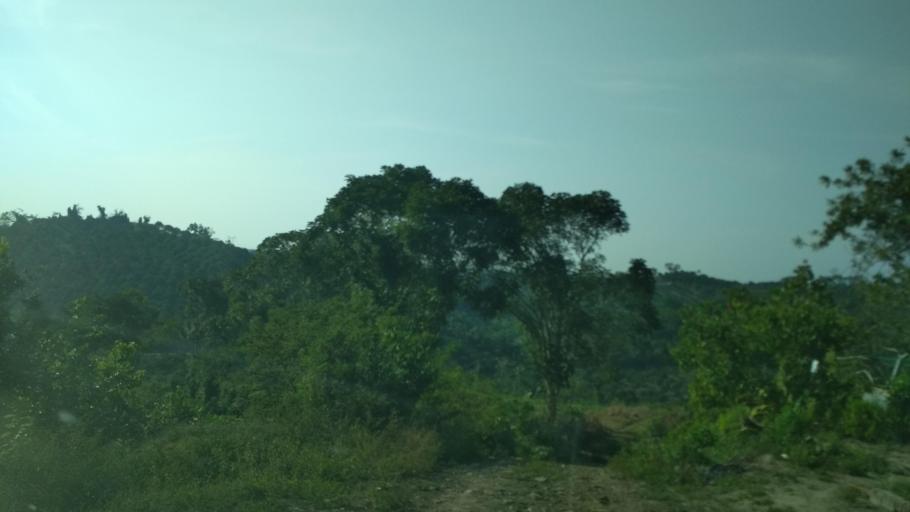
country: MX
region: Puebla
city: San Jose Acateno
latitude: 20.2172
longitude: -97.2647
